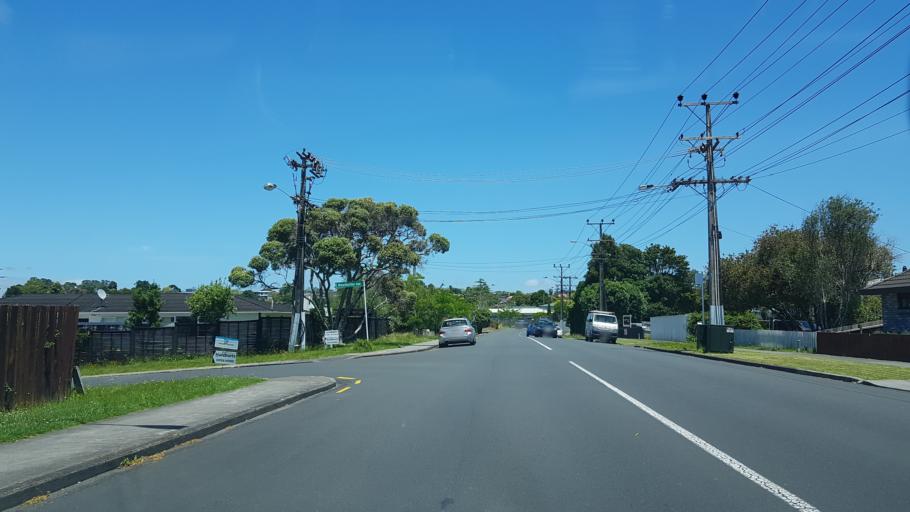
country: NZ
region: Auckland
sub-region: Auckland
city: North Shore
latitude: -36.7905
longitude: 174.7301
